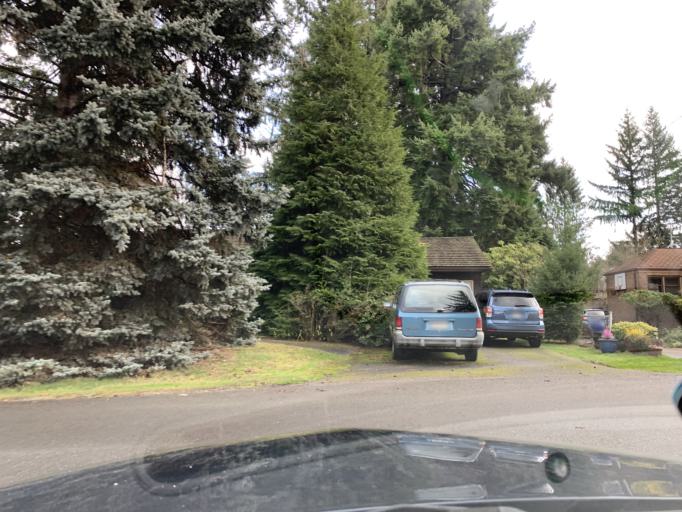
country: US
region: Washington
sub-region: King County
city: Mercer Island
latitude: 47.5863
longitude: -122.2449
